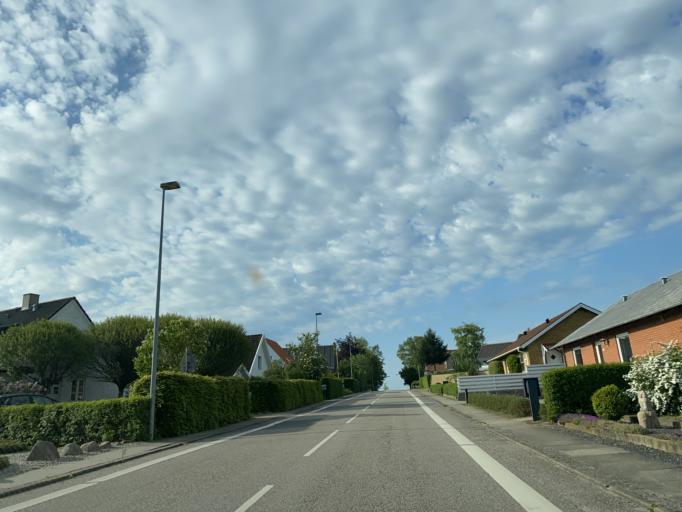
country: DK
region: South Denmark
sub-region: Sonderborg Kommune
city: Dybbol
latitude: 54.9109
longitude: 9.7656
